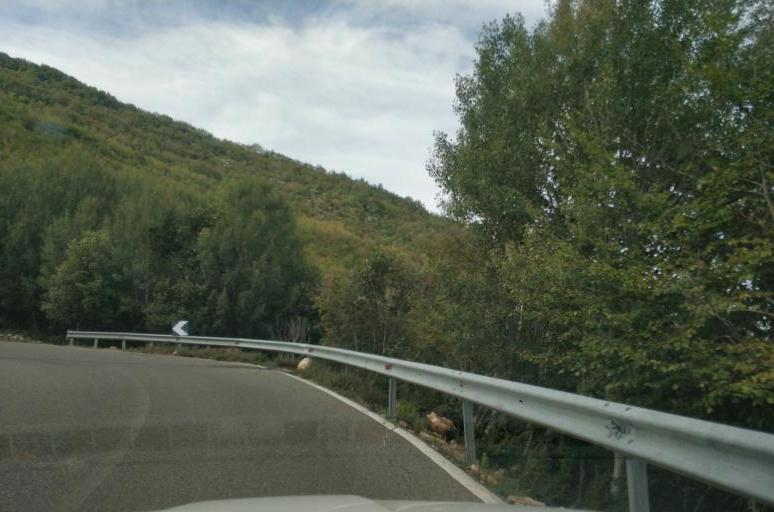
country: AL
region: Durres
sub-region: Rrethi i Krujes
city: Kruje
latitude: 41.5240
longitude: 19.8018
